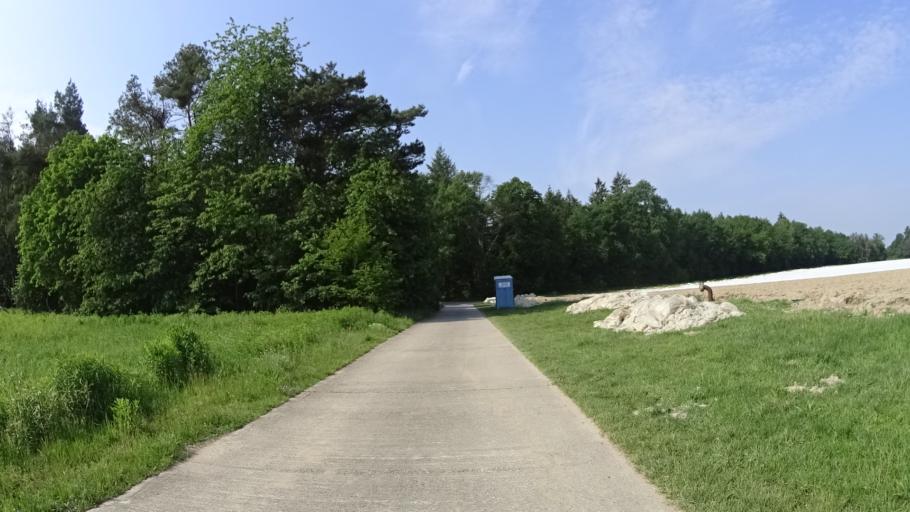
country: DE
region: Baden-Wuerttemberg
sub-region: Karlsruhe Region
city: Hambrucken
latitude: 49.2032
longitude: 8.5188
